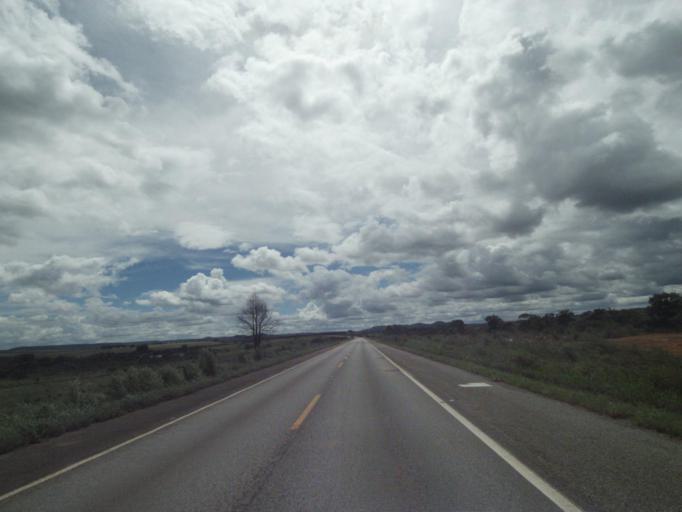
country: BR
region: Goias
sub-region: Pirenopolis
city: Pirenopolis
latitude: -15.7490
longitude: -48.6584
